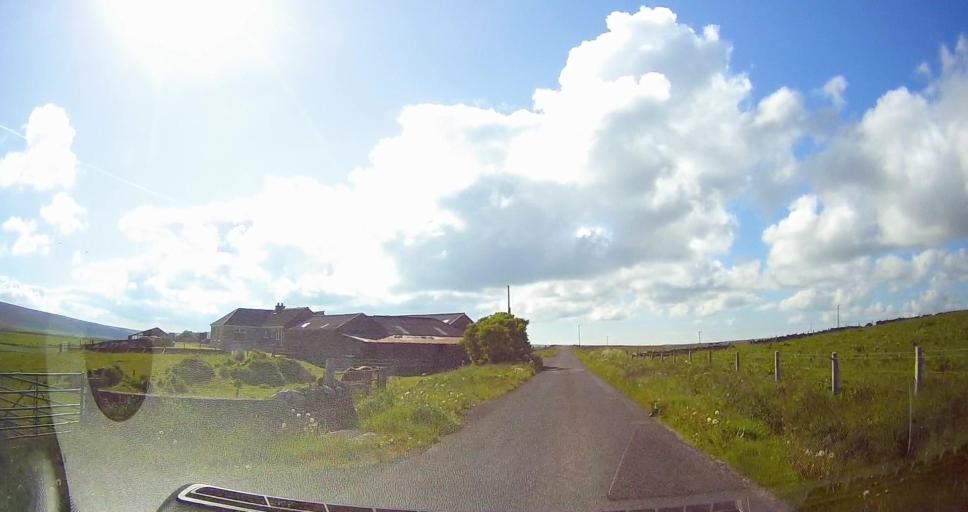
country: GB
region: Scotland
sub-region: Orkney Islands
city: Stromness
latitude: 58.9872
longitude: -3.1482
